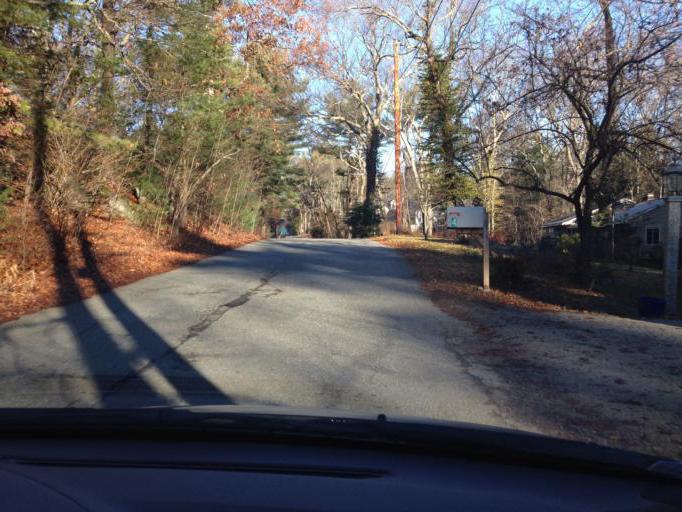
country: US
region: Massachusetts
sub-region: Middlesex County
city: Bedford
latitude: 42.5126
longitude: -71.2777
